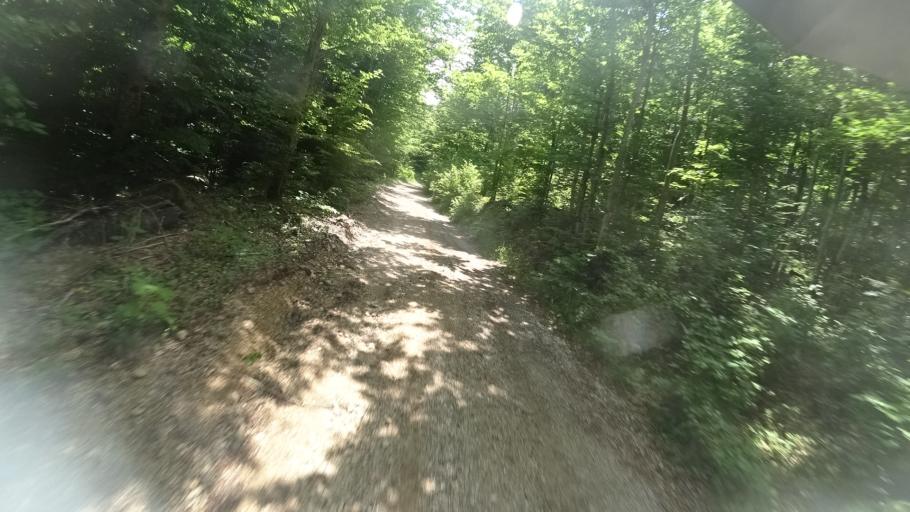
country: HR
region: Zadarska
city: Gracac
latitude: 44.4944
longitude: 15.8750
